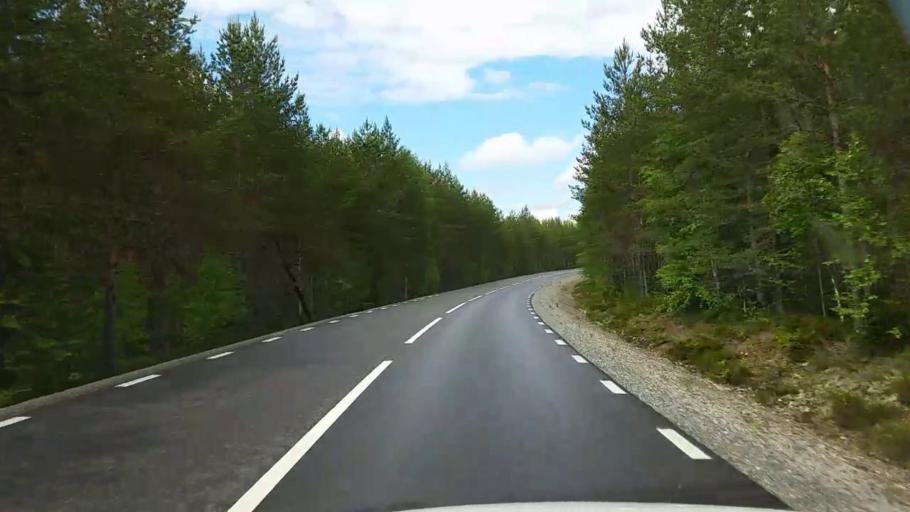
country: SE
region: Gaevleborg
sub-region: Sandvikens Kommun
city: Jarbo
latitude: 60.8802
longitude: 16.3863
